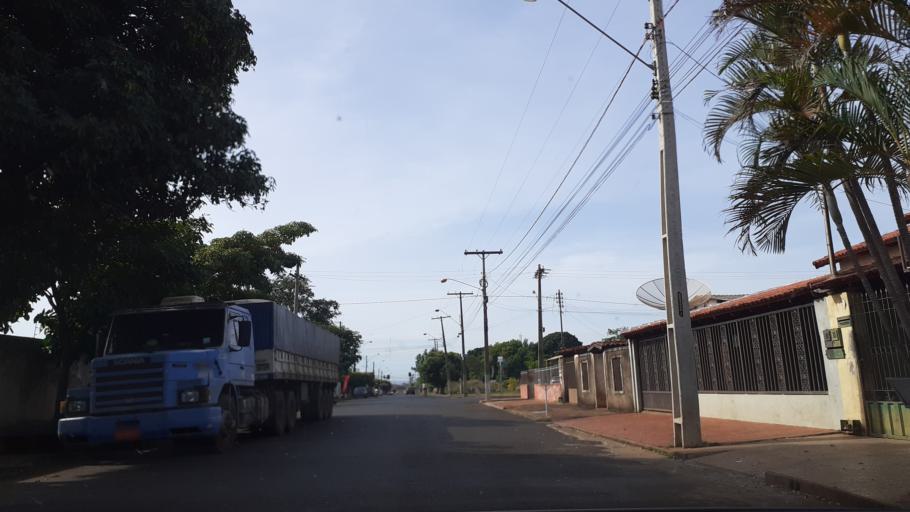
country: BR
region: Goias
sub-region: Itumbiara
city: Itumbiara
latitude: -18.4159
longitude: -49.2414
